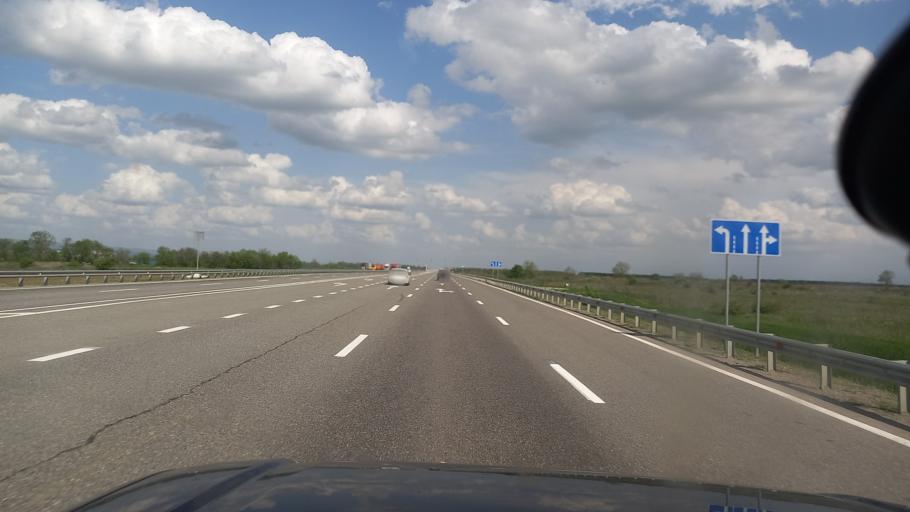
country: RU
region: Ingushetiya
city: Ordzhonikidzevskaya
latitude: 43.2809
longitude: 45.0863
